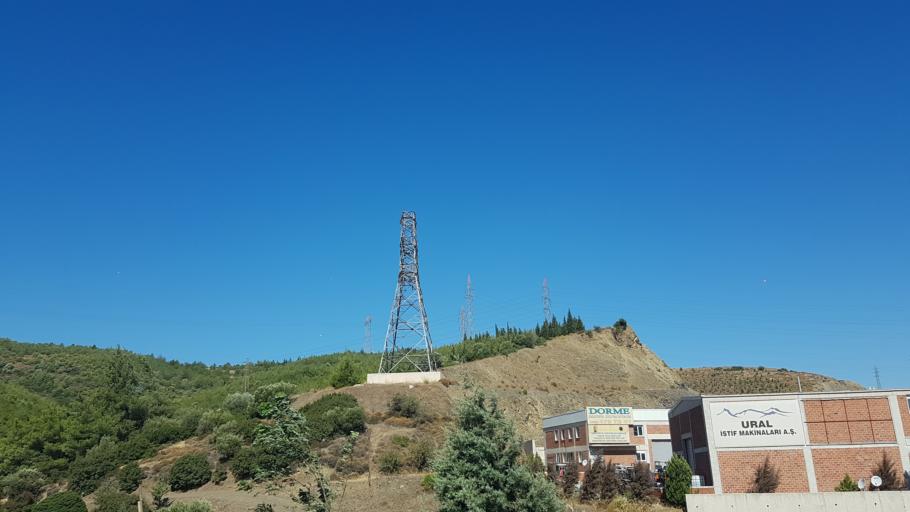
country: TR
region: Izmir
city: Bornova
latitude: 38.4112
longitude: 27.2372
